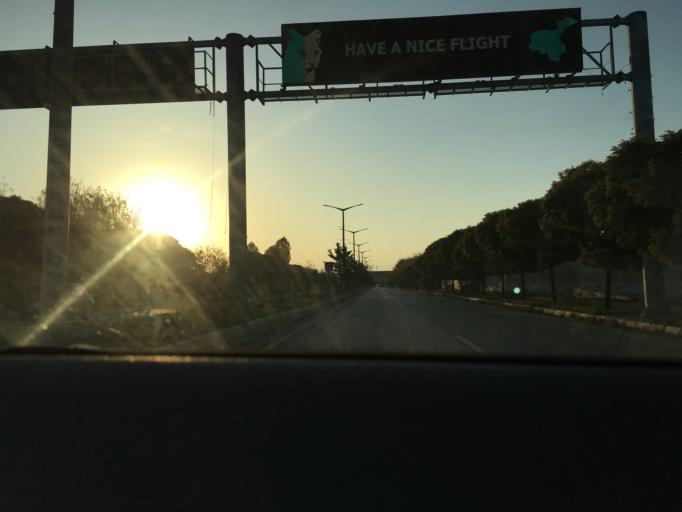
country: TR
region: Van
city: Van
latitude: 38.4698
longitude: 43.3448
